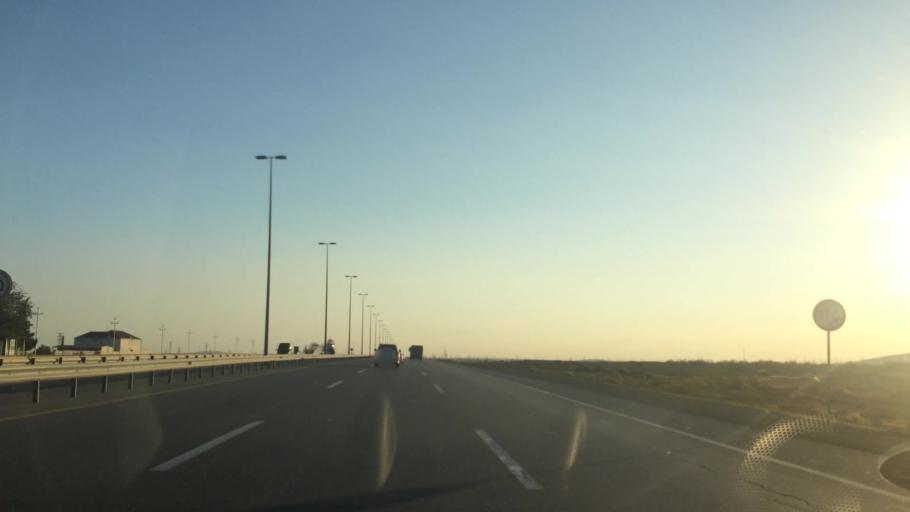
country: AZ
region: Baki
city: Qobustan
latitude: 39.9888
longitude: 49.4285
